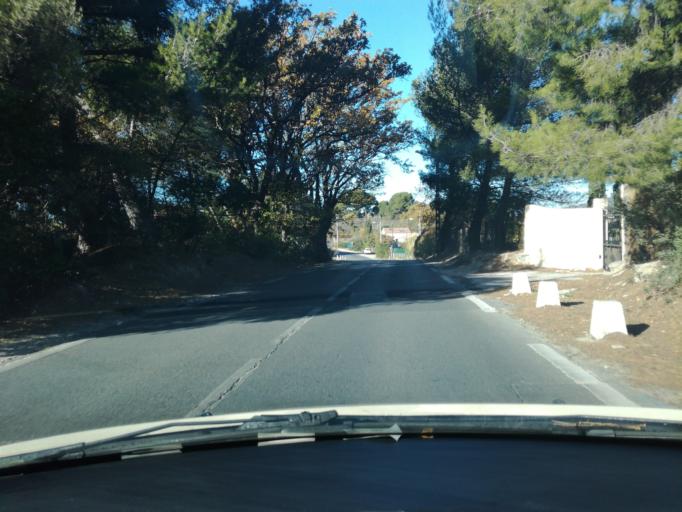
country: FR
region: Provence-Alpes-Cote d'Azur
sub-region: Departement des Bouches-du-Rhone
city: Allauch
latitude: 43.3287
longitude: 5.4794
